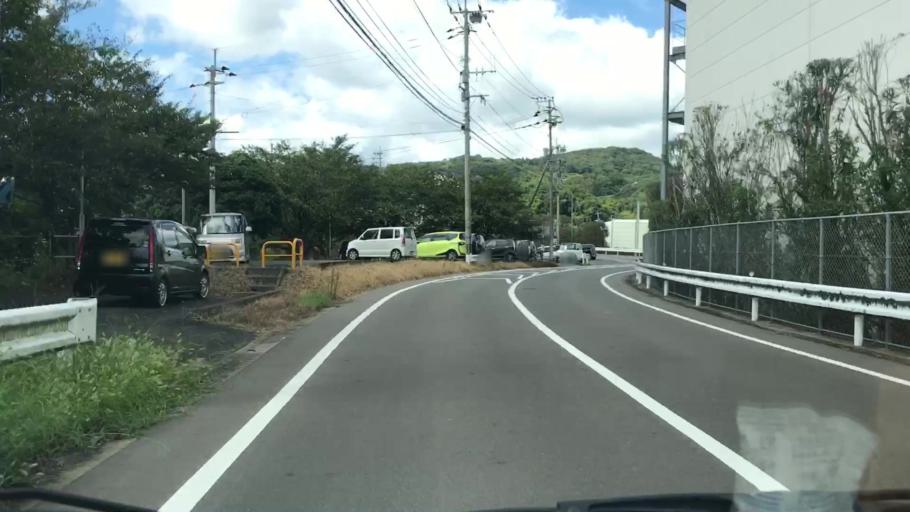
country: JP
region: Saga Prefecture
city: Takeocho-takeo
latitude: 33.2301
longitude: 130.1407
